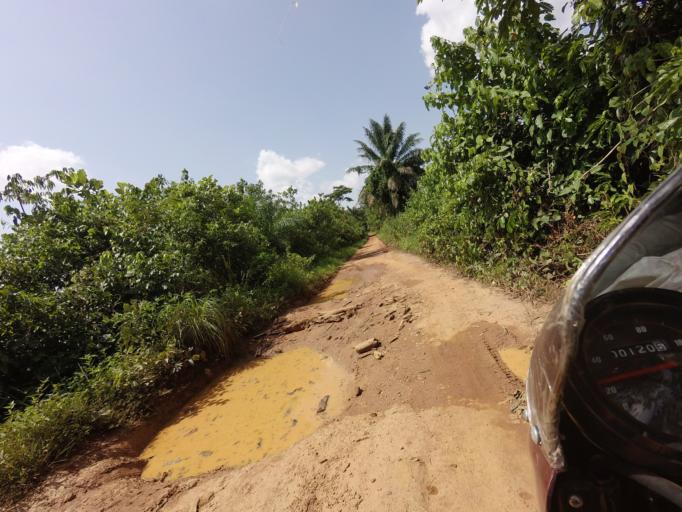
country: SL
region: Eastern Province
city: Manowa
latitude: 8.1622
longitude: -10.7520
